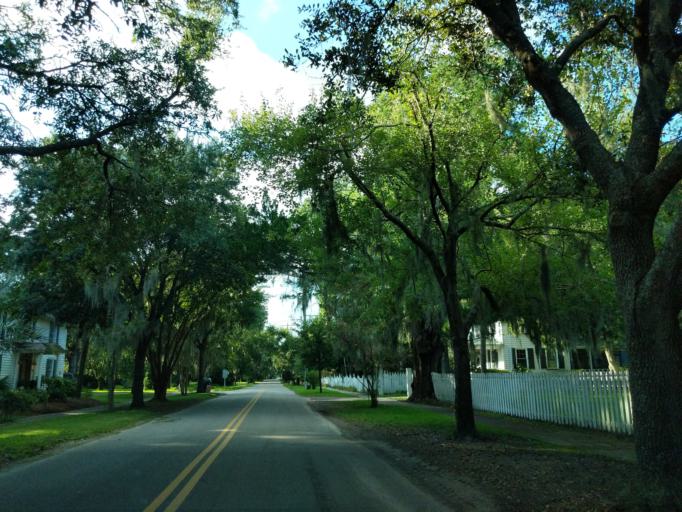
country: US
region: South Carolina
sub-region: Charleston County
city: Awendaw
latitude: 33.0820
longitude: -79.4590
